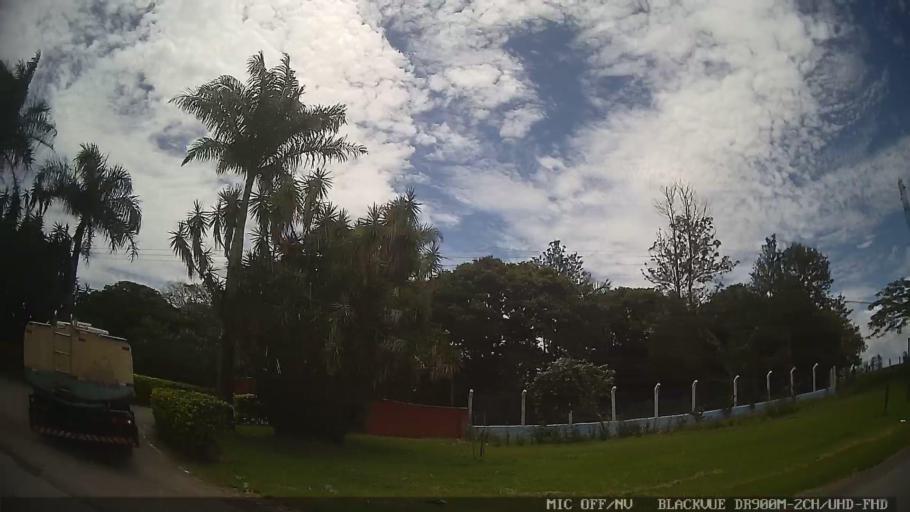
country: BR
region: Sao Paulo
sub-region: Conchas
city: Conchas
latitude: -23.0612
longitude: -47.9678
